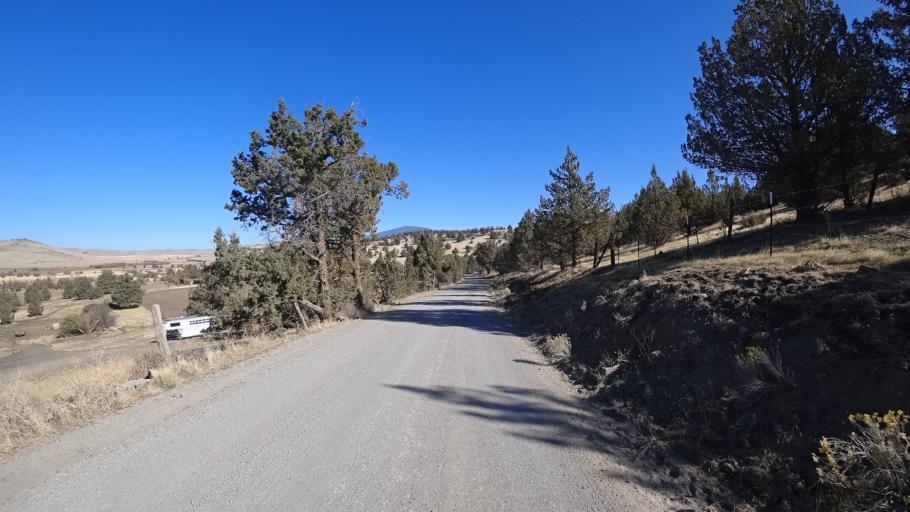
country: US
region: California
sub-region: Siskiyou County
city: Montague
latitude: 41.7144
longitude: -122.3747
